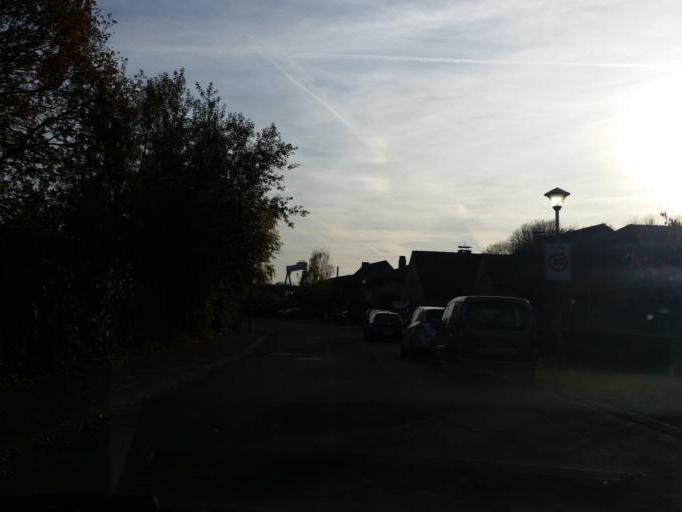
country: BE
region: Flanders
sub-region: Provincie Antwerpen
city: Hoboken
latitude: 51.1884
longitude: 4.3393
